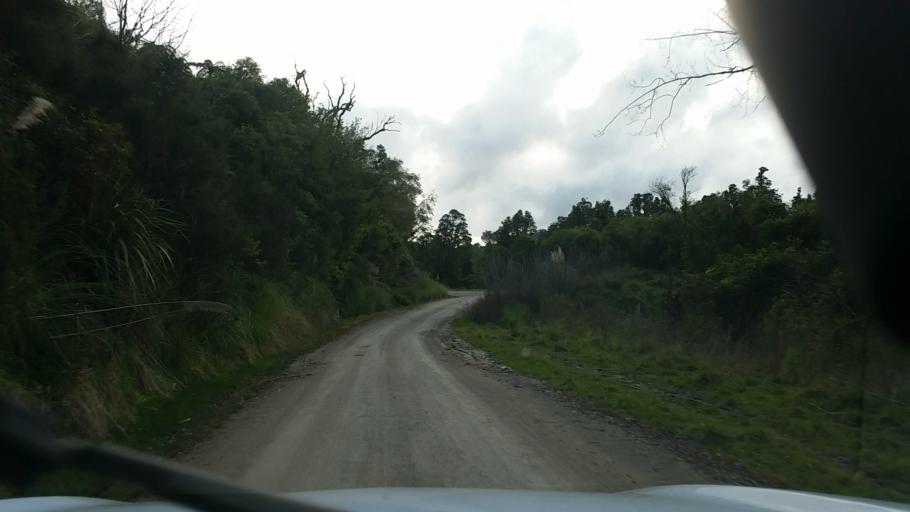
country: NZ
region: Taranaki
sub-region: South Taranaki District
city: Patea
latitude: -39.5567
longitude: 174.8036
